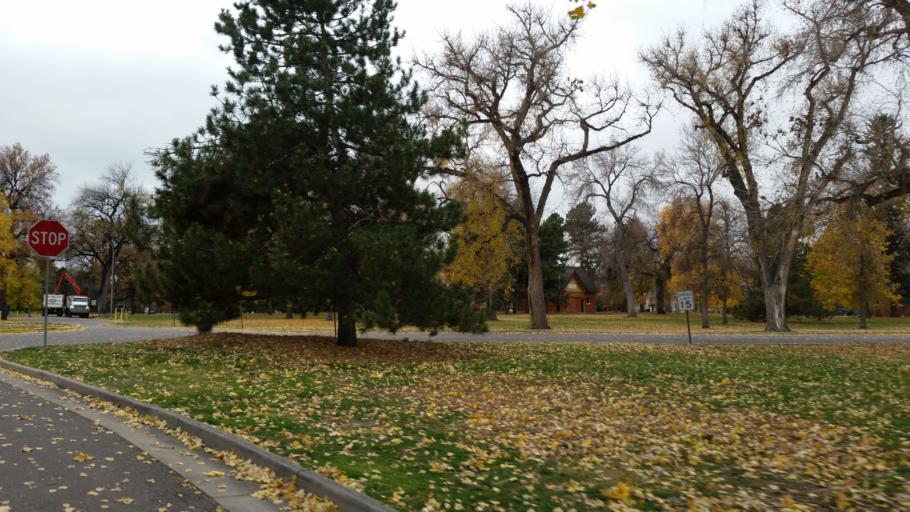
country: US
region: Colorado
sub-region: Denver County
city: Denver
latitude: 39.7481
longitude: -104.9579
